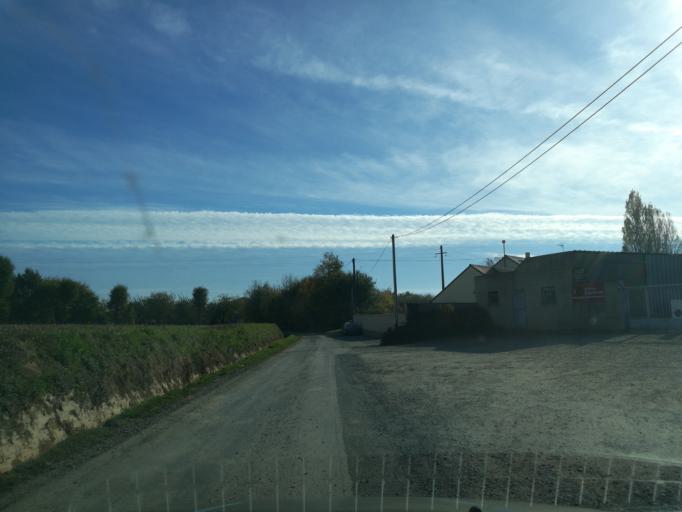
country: FR
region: Brittany
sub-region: Departement d'Ille-et-Vilaine
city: Bedee
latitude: 48.1681
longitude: -1.9430
